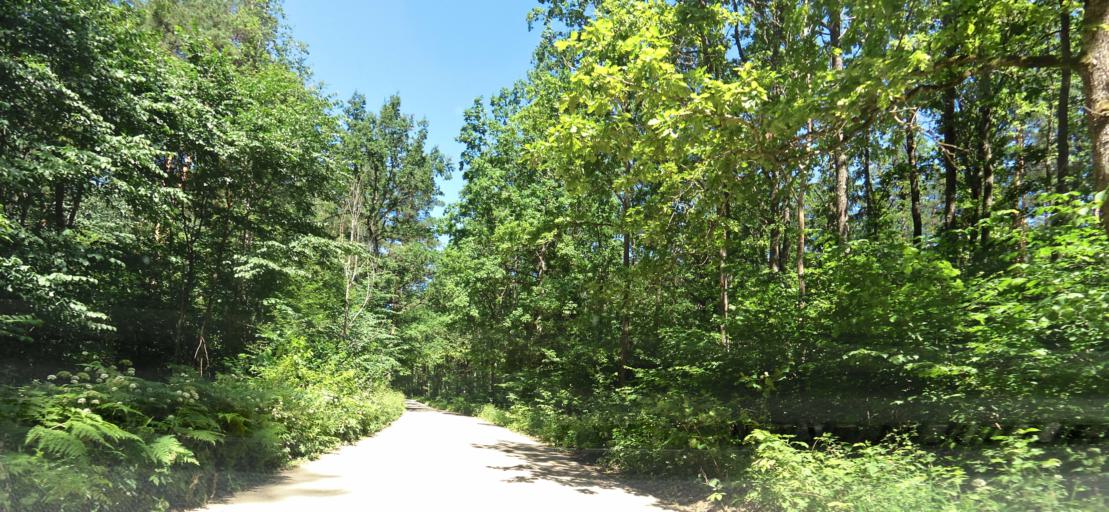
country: LT
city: Grigiskes
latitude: 54.7978
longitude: 24.9828
